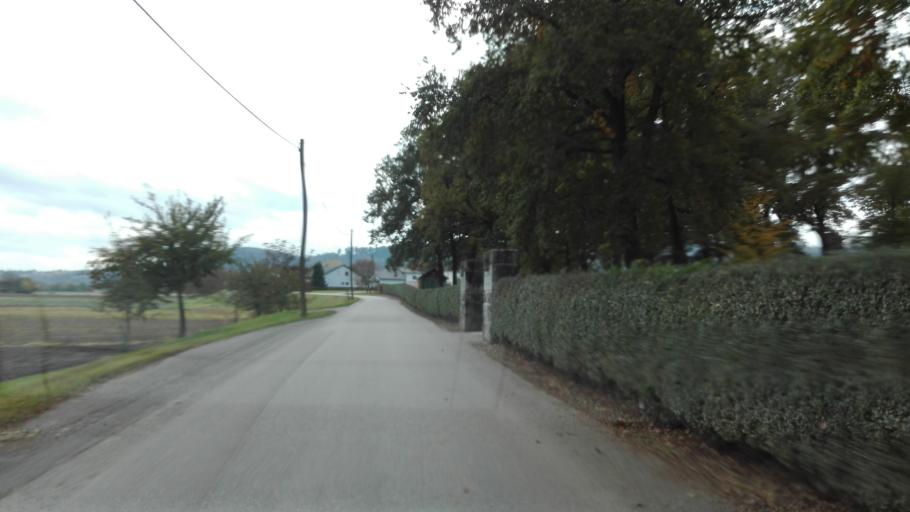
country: AT
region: Upper Austria
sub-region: Politischer Bezirk Urfahr-Umgebung
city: Feldkirchen an der Donau
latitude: 48.3500
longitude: 14.0096
